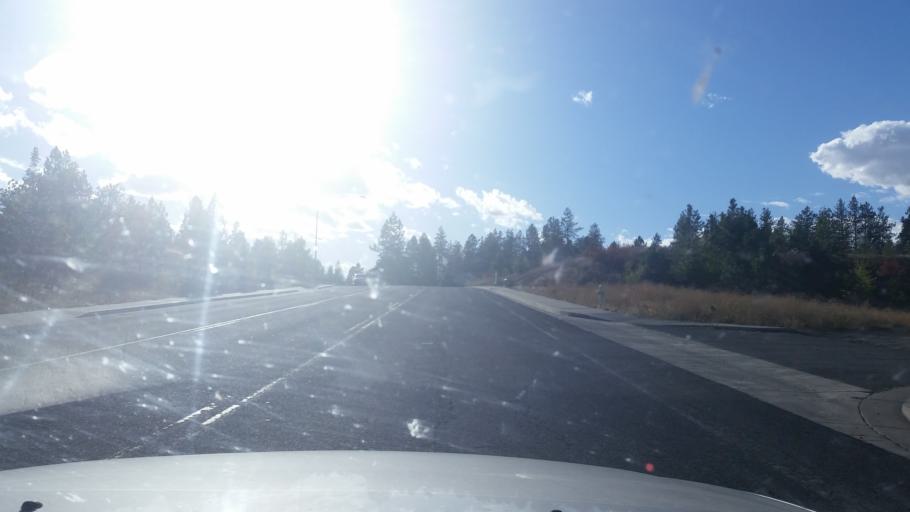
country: US
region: Washington
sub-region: Spokane County
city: Cheney
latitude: 47.5040
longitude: -117.5663
